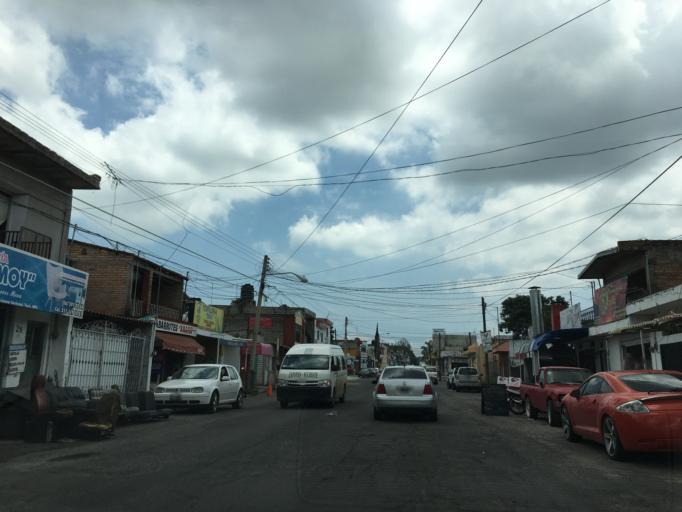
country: MX
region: Nayarit
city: Xalisco
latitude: 21.4784
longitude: -104.8881
